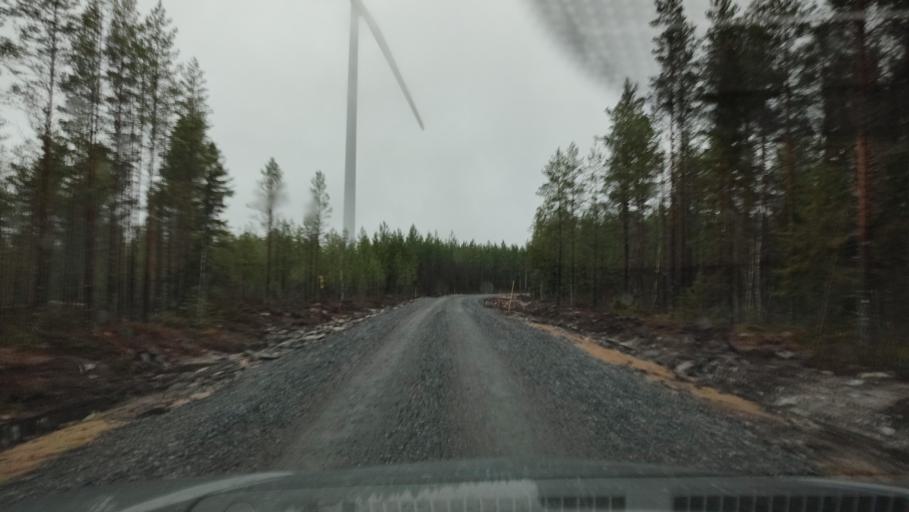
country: FI
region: Southern Ostrobothnia
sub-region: Suupohja
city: Karijoki
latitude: 62.1466
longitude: 21.6134
